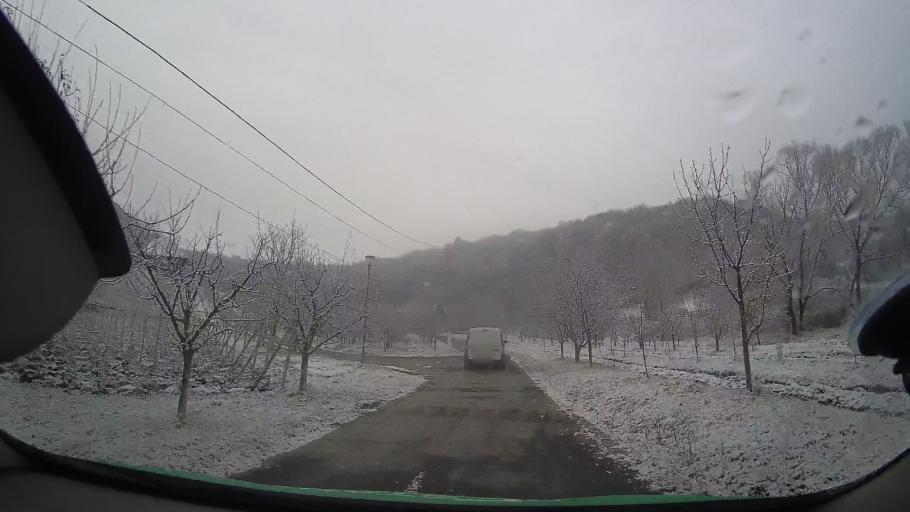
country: RO
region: Sibiu
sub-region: Comuna Darlos
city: Darlos
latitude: 46.1585
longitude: 24.3808
